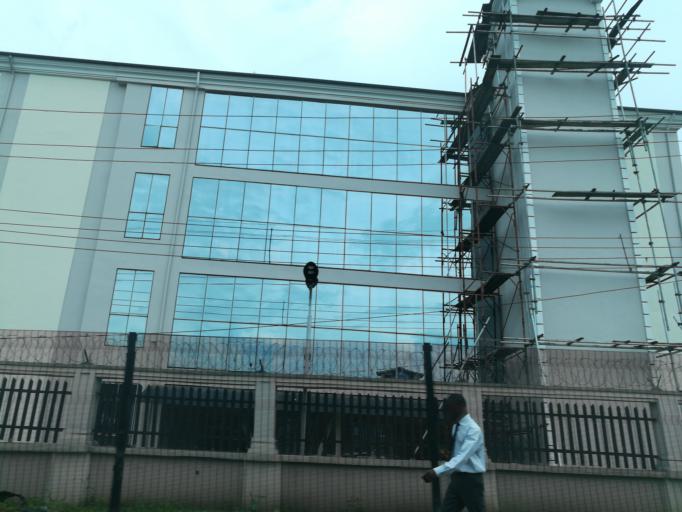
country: NG
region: Rivers
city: Port Harcourt
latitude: 4.7899
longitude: 7.0027
